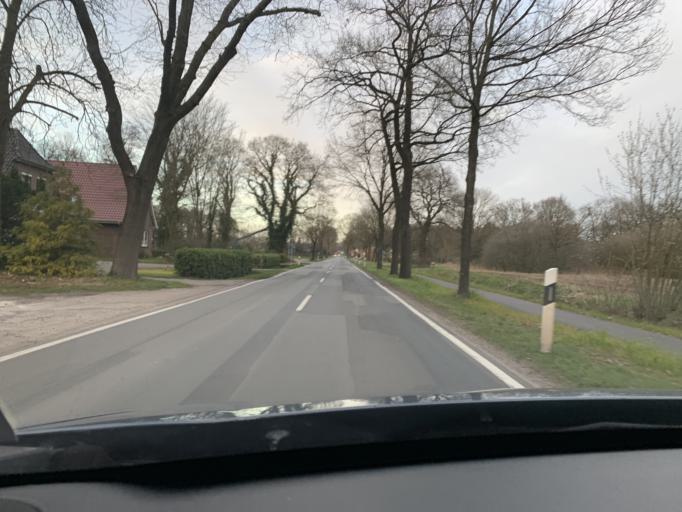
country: DE
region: Lower Saxony
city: Apen
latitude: 53.1953
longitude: 7.8740
